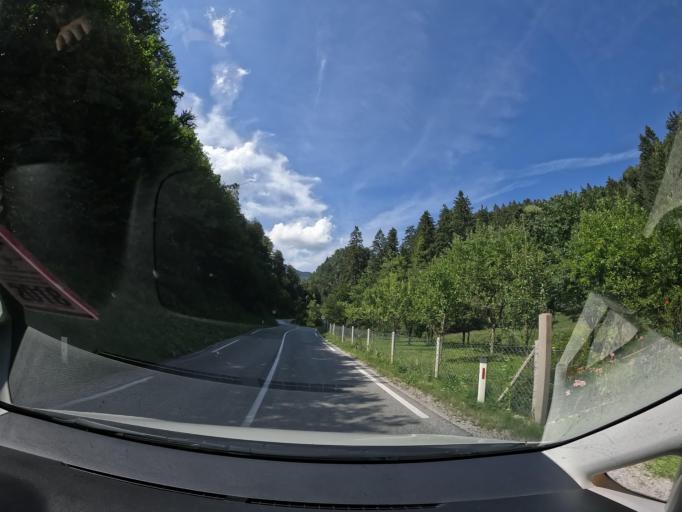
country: SI
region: Kranj
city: Golnik
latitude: 46.3838
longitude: 14.3788
